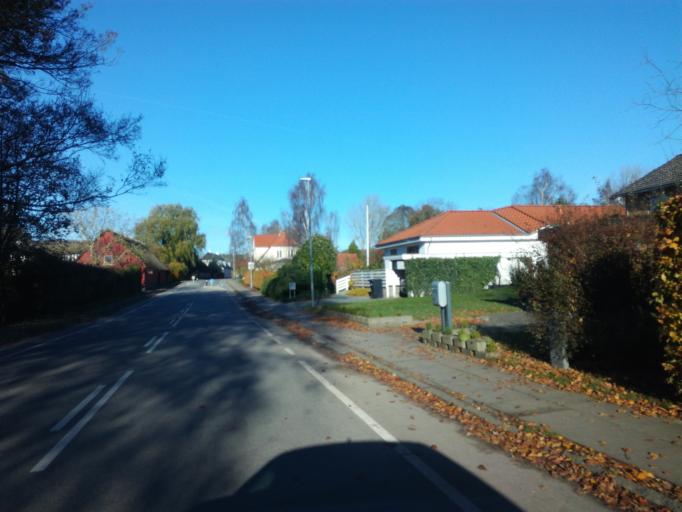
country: DK
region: South Denmark
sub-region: Vejle Kommune
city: Vejle
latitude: 55.6717
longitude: 9.5750
